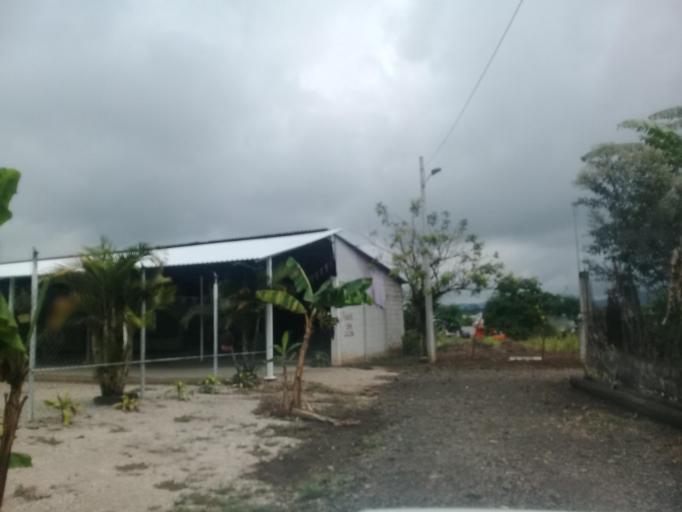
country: MX
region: Veracruz
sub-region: Cordoba
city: San Jose de Tapia
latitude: 18.8406
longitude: -96.9560
